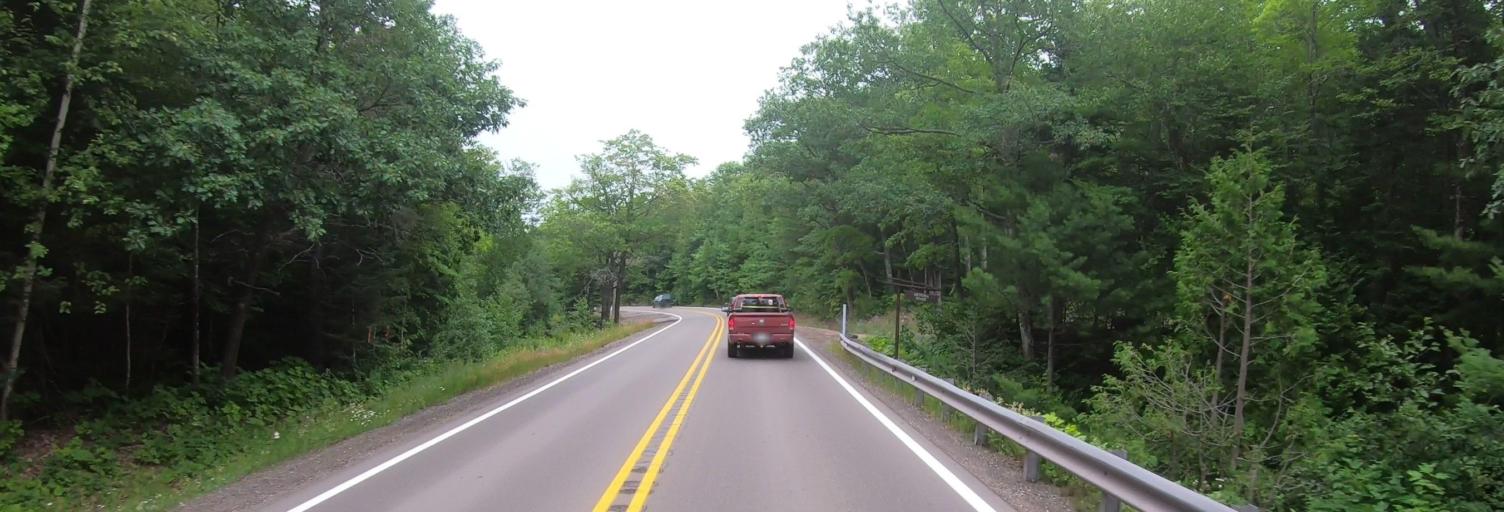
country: US
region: Michigan
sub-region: Keweenaw County
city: Eagle River
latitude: 47.4296
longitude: -87.9831
